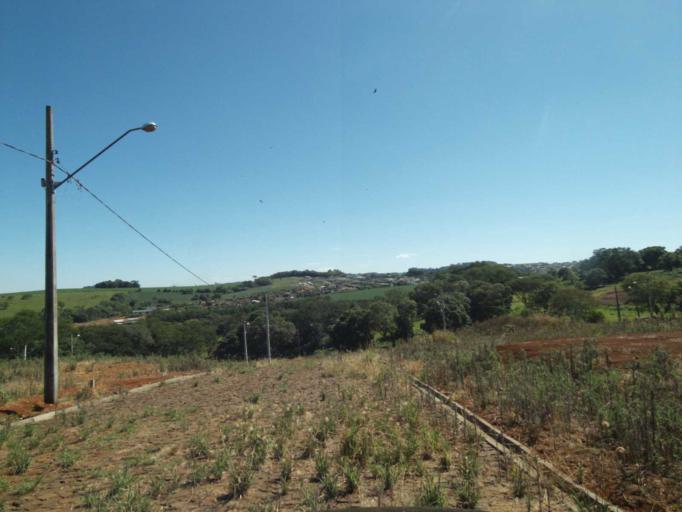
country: BR
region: Parana
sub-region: Coronel Vivida
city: Coronel Vivida
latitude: -25.9616
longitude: -52.8061
